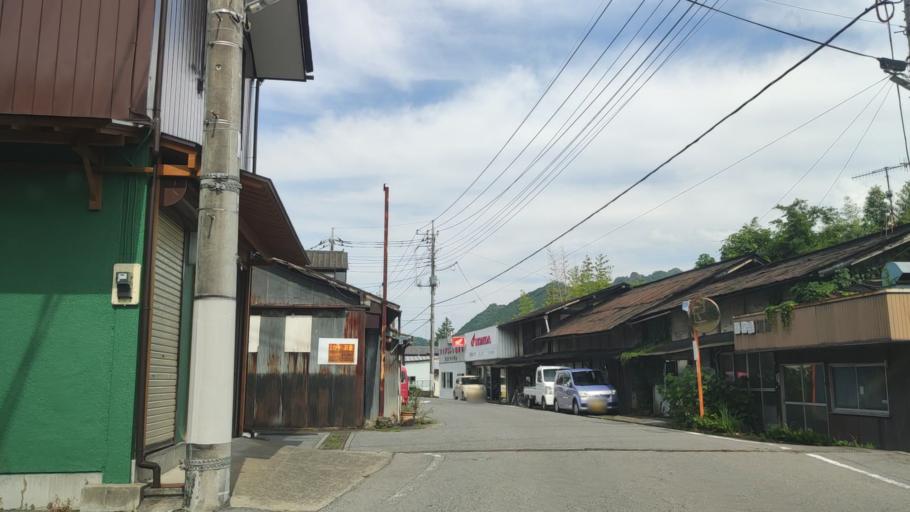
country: JP
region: Gunma
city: Tomioka
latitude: 36.2101
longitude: 138.7844
